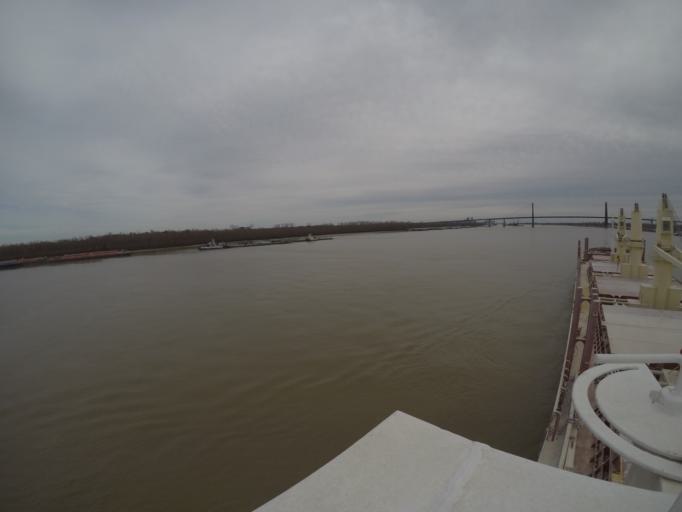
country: US
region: Louisiana
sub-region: Saint Charles Parish
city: Luling
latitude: 29.9487
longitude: -90.3895
